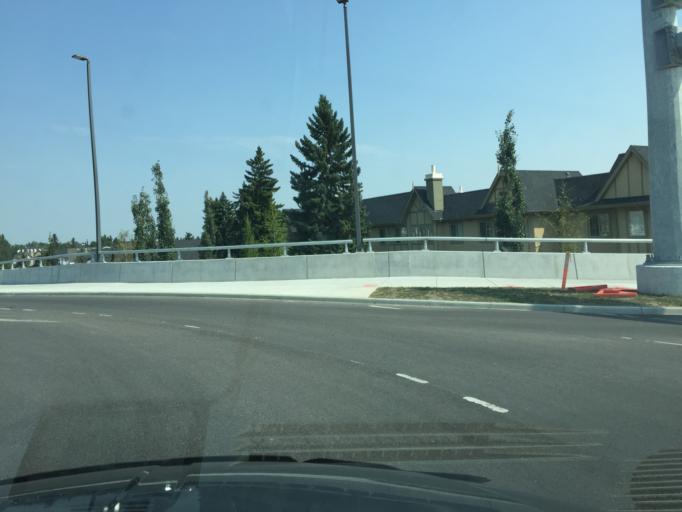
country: CA
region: Alberta
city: Calgary
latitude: 51.0157
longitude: -114.1154
